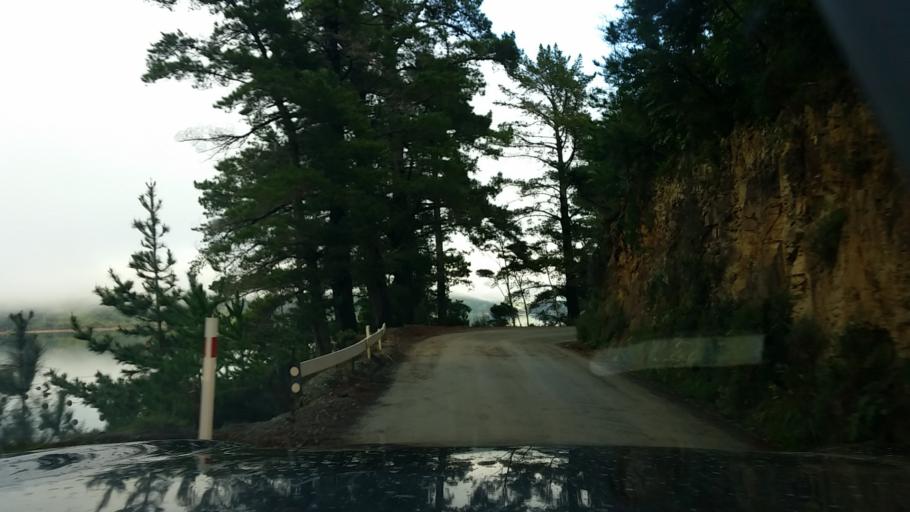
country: NZ
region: Marlborough
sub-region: Marlborough District
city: Picton
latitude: -41.1782
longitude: 174.0653
